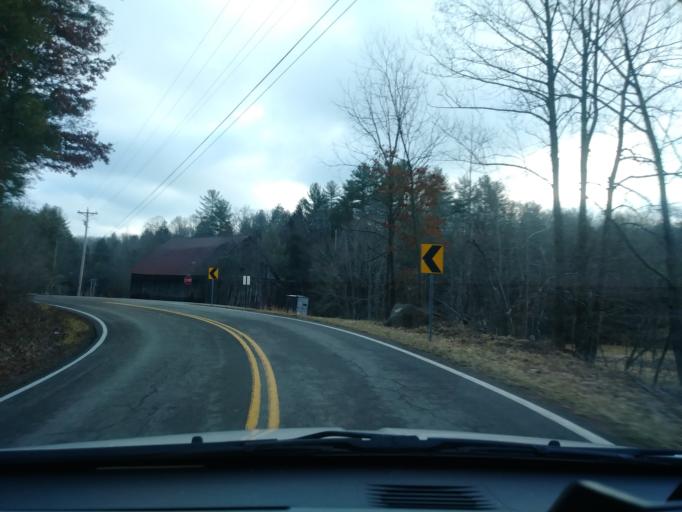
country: US
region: Tennessee
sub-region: Unicoi County
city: Unicoi
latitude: 36.2026
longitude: -82.2370
